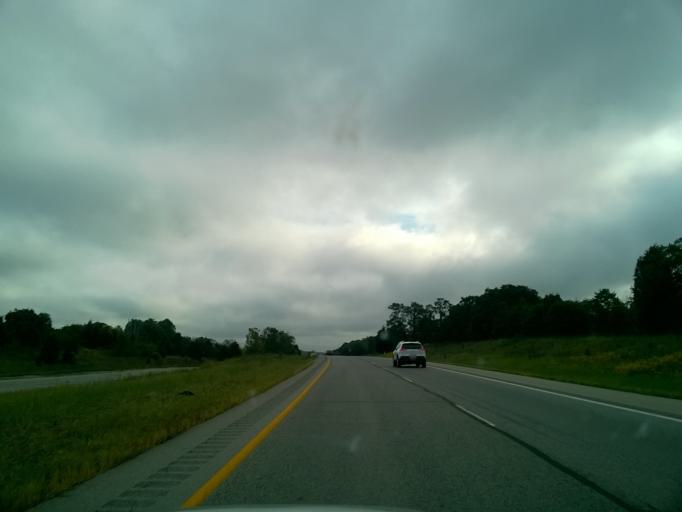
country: US
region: Indiana
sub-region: Crawford County
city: English
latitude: 38.2453
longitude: -86.3489
